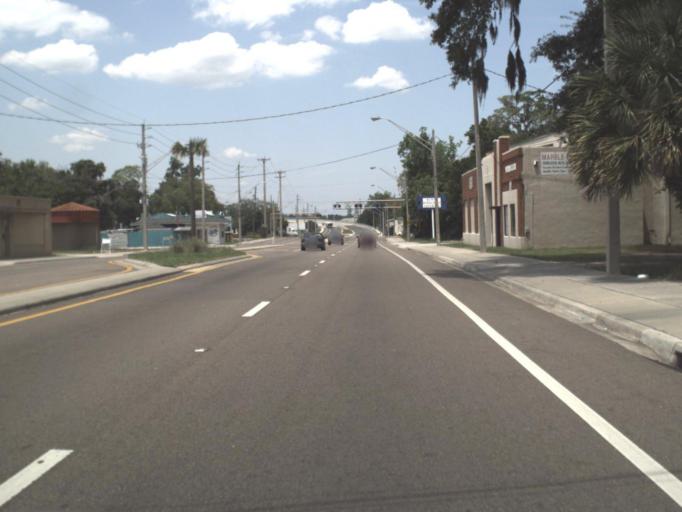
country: US
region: Florida
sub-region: Duval County
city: Jacksonville
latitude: 30.3868
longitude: -81.6484
